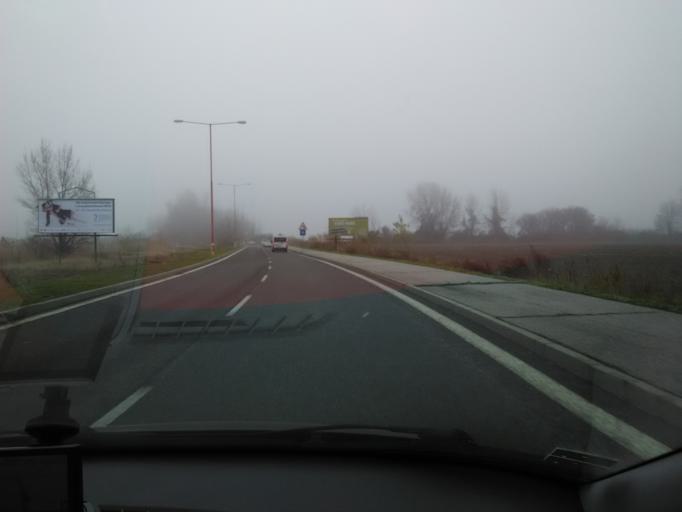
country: AT
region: Burgenland
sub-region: Politischer Bezirk Neusiedl am See
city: Kittsee
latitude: 48.1168
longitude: 17.0763
